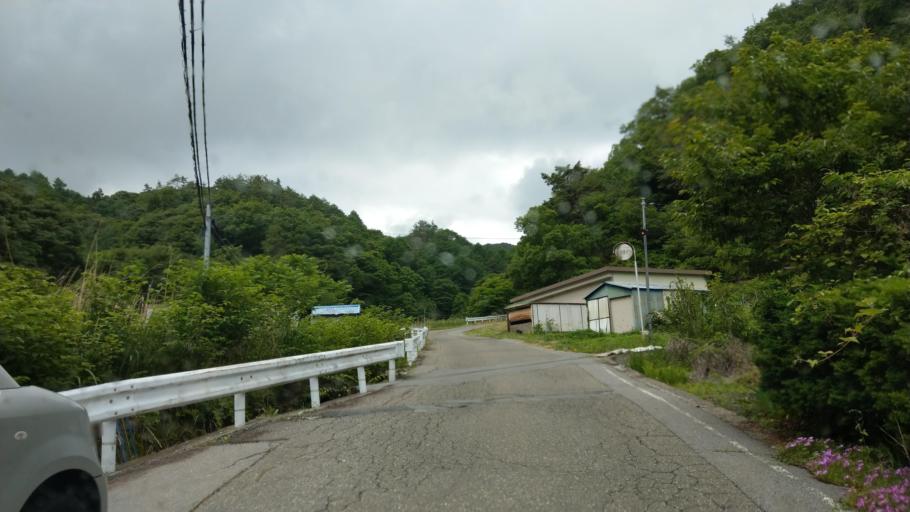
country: JP
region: Nagano
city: Komoro
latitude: 36.3163
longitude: 138.4124
